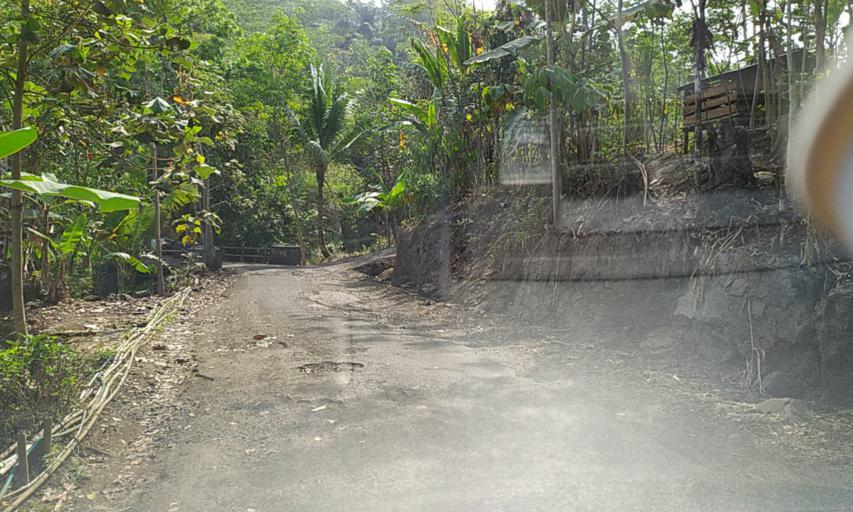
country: ID
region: Central Java
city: Pasirmanggu
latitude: -7.2266
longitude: 108.5947
